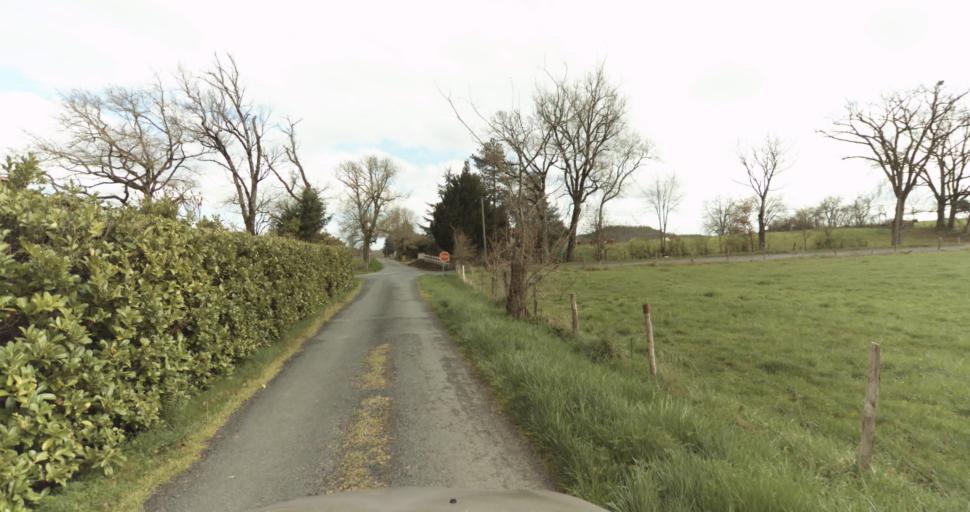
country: FR
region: Midi-Pyrenees
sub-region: Departement du Tarn
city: Frejairolles
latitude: 43.8841
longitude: 2.2007
